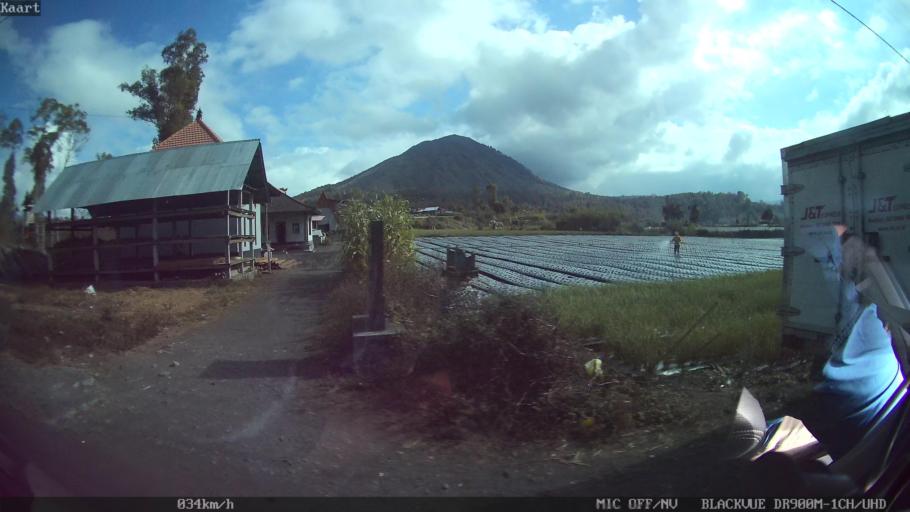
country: ID
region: Bali
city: Banjar Trunyan
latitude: -8.2196
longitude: 115.3924
